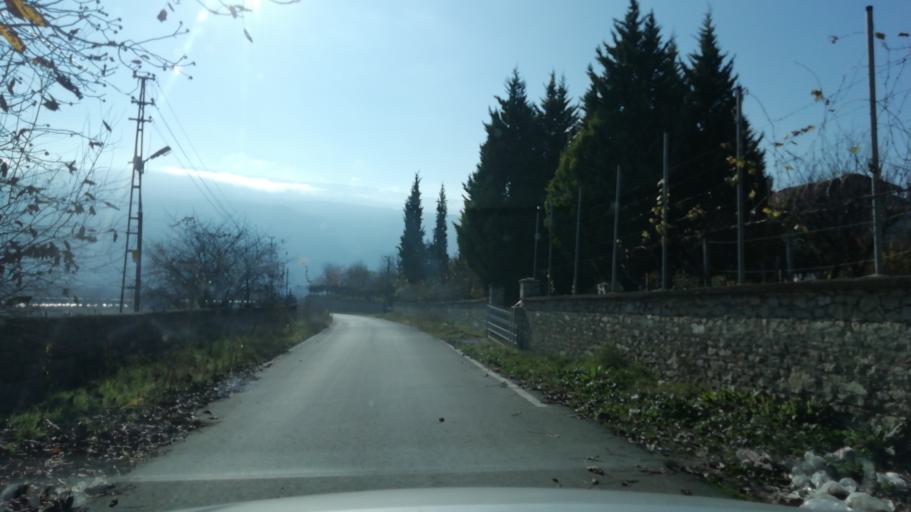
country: TR
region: Karabuk
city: Safranbolu
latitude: 41.2286
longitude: 32.7808
